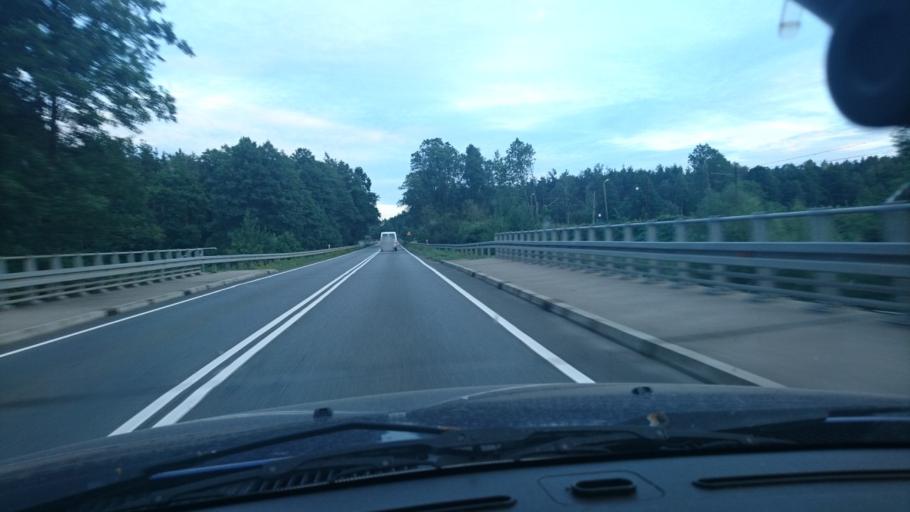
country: PL
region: Silesian Voivodeship
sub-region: Powiat tarnogorski
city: Tworog
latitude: 50.5259
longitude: 18.7190
